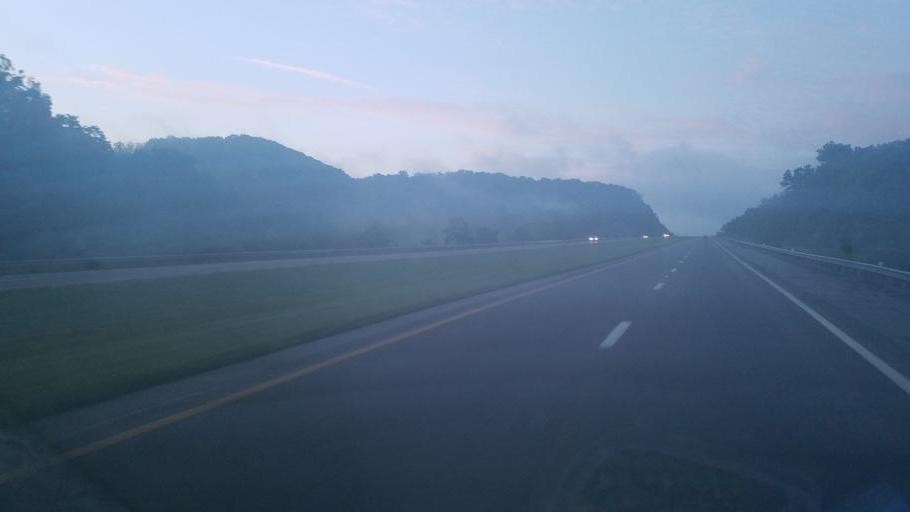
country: US
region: Ohio
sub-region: Ross County
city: Chillicothe
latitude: 39.2381
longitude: -82.8390
